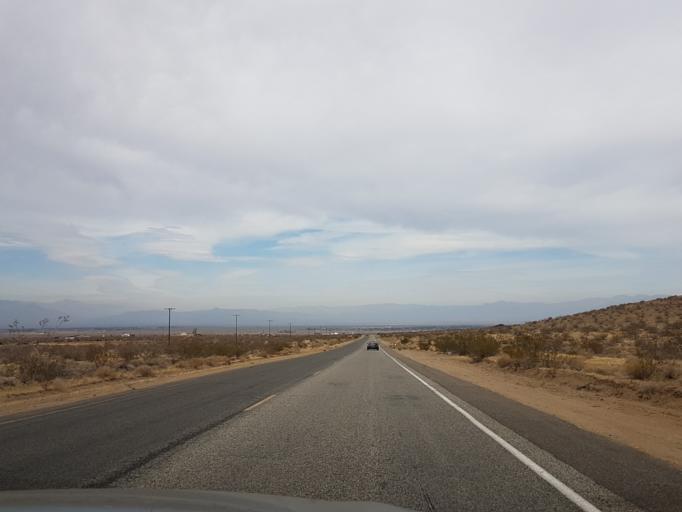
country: US
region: California
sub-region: Kern County
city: Ridgecrest
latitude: 35.5606
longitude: -117.7138
